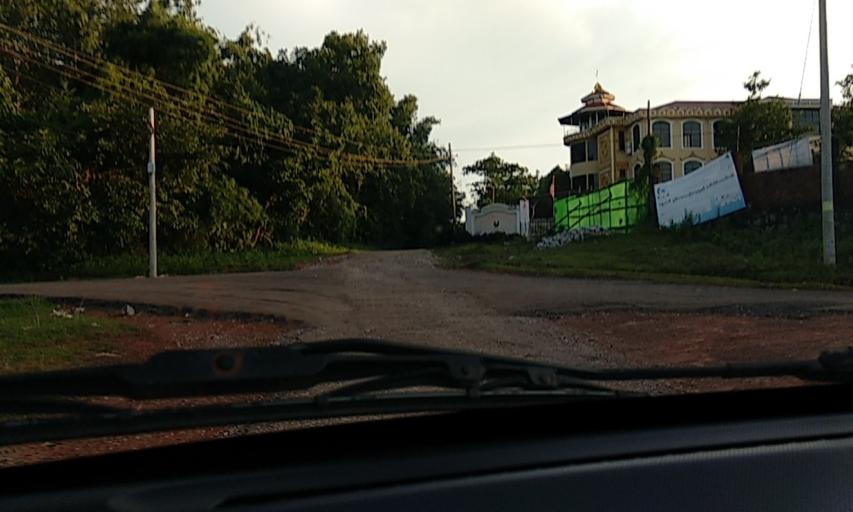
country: MM
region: Mon
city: Mawlamyine
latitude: 16.4560
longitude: 97.6504
